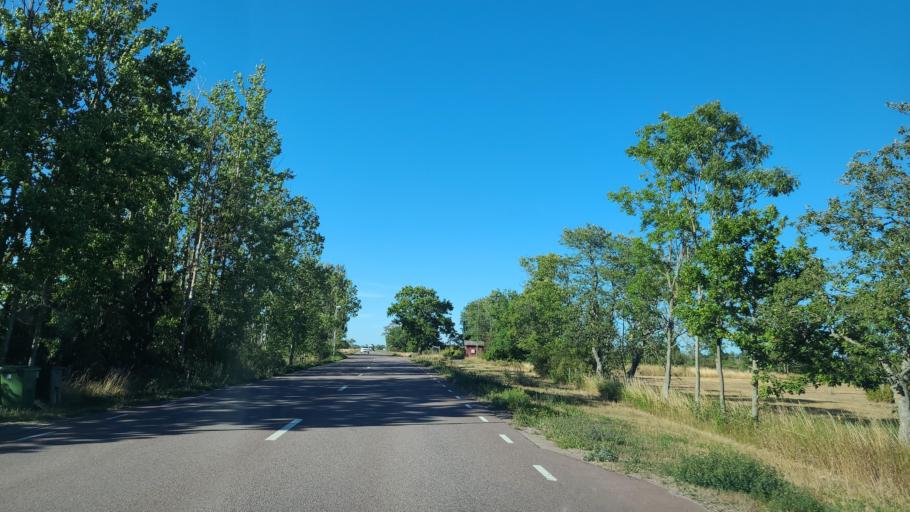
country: SE
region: Kalmar
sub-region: Borgholms Kommun
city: Borgholm
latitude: 57.2137
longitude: 17.0465
